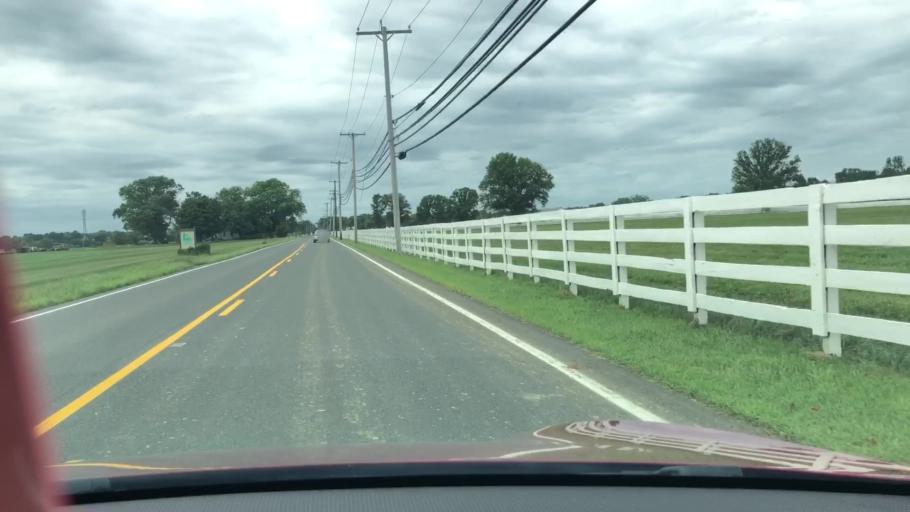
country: US
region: New Jersey
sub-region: Monmouth County
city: Shrewsbury
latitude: 40.1679
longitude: -74.5189
